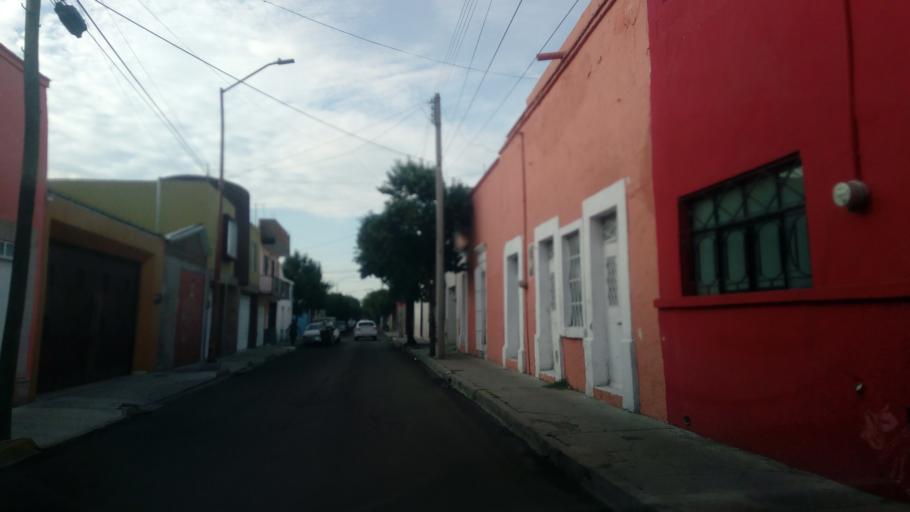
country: MX
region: Durango
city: Victoria de Durango
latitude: 24.0322
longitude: -104.6690
